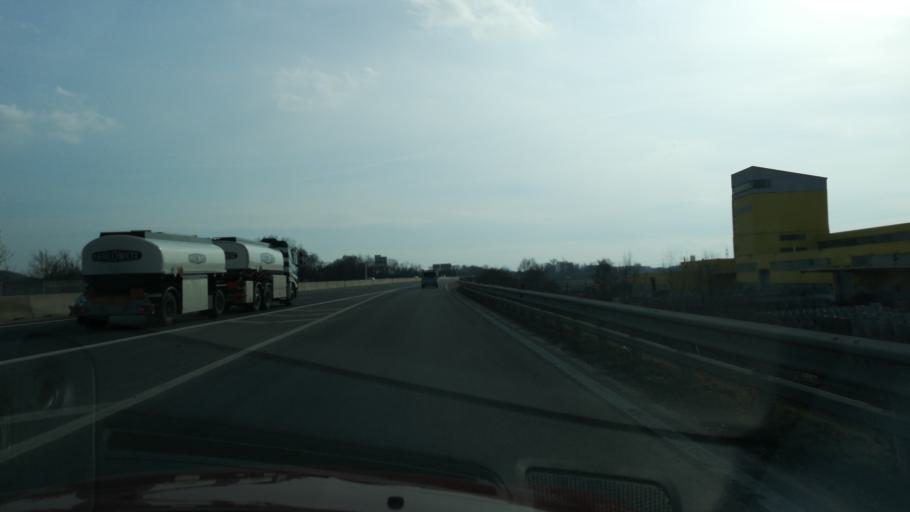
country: AT
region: Lower Austria
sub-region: Politischer Bezirk Sankt Polten
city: Traismauer
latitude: 48.3415
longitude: 15.7233
